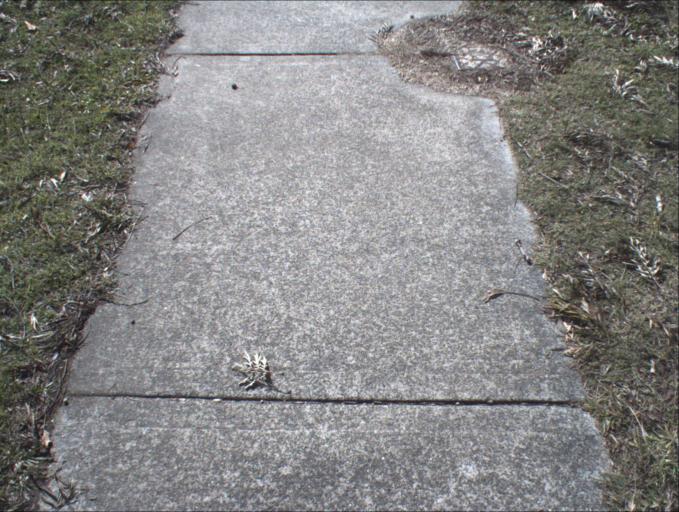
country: AU
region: Queensland
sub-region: Logan
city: Logan Reserve
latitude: -27.6821
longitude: 153.0916
